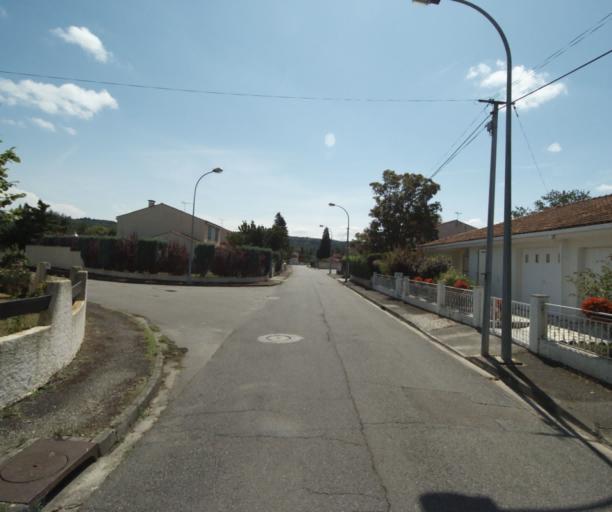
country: FR
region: Midi-Pyrenees
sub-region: Departement de la Haute-Garonne
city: Revel
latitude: 43.4603
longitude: 2.0164
